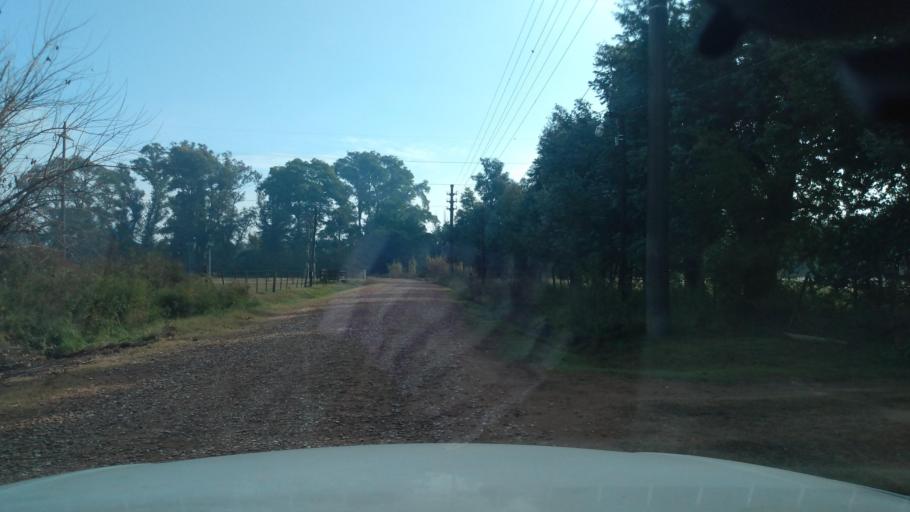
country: AR
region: Buenos Aires
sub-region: Partido de Lujan
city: Lujan
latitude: -34.5867
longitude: -59.1276
